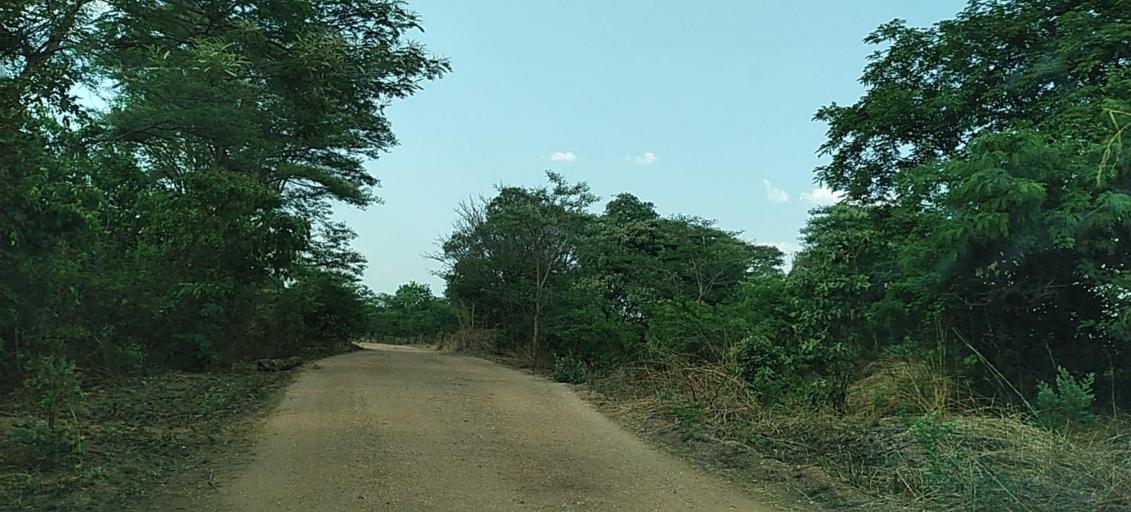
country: ZM
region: Copperbelt
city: Mpongwe
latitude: -13.4827
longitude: 28.0842
